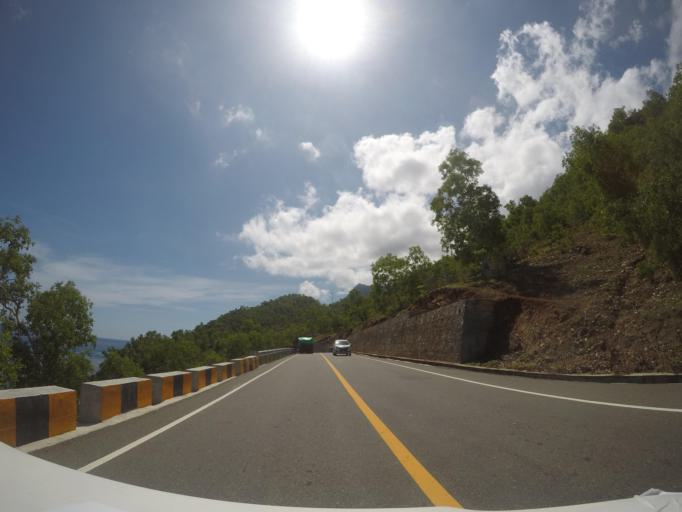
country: TL
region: Manatuto
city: Manatuto
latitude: -8.4763
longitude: 125.8950
